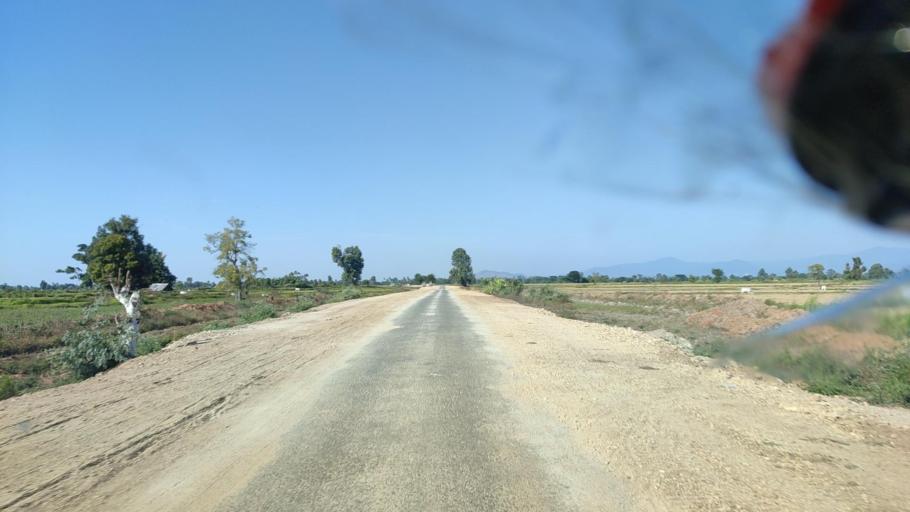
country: MM
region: Mandalay
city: Yamethin
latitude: 20.1307
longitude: 96.2712
